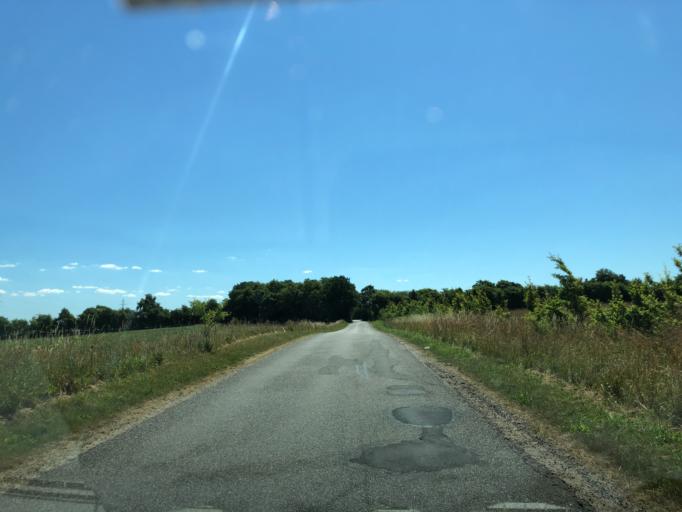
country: DK
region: Central Jutland
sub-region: Viborg Kommune
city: Viborg
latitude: 56.5220
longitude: 9.4858
